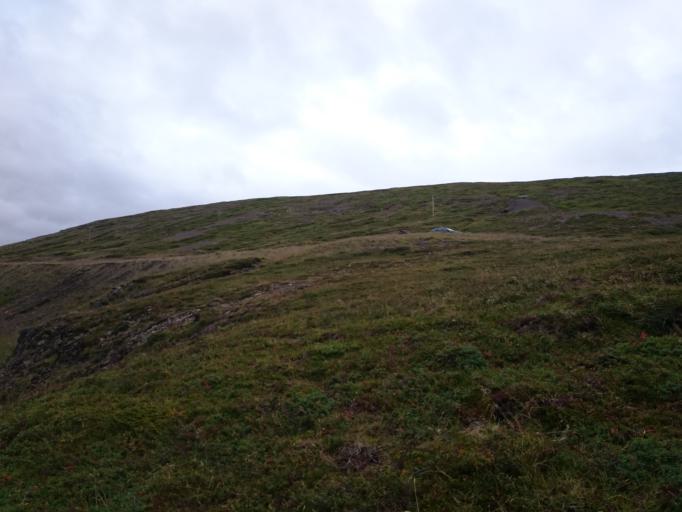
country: IS
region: West
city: Borgarnes
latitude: 65.2618
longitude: -21.7626
